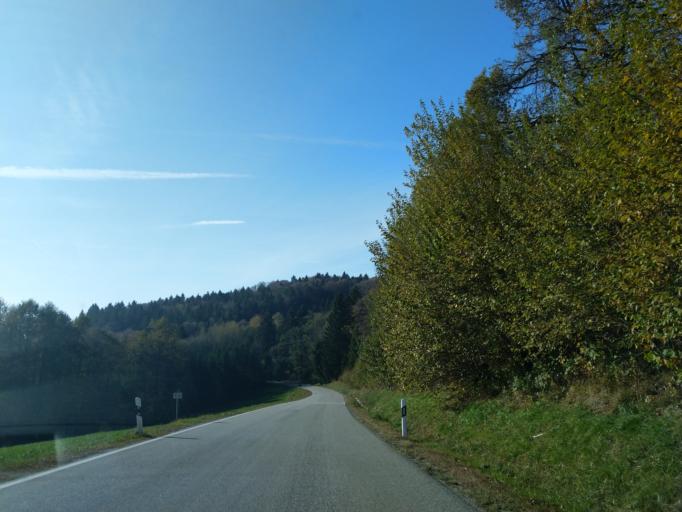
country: DE
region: Bavaria
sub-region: Lower Bavaria
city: Hunding
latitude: 48.8143
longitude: 13.1892
